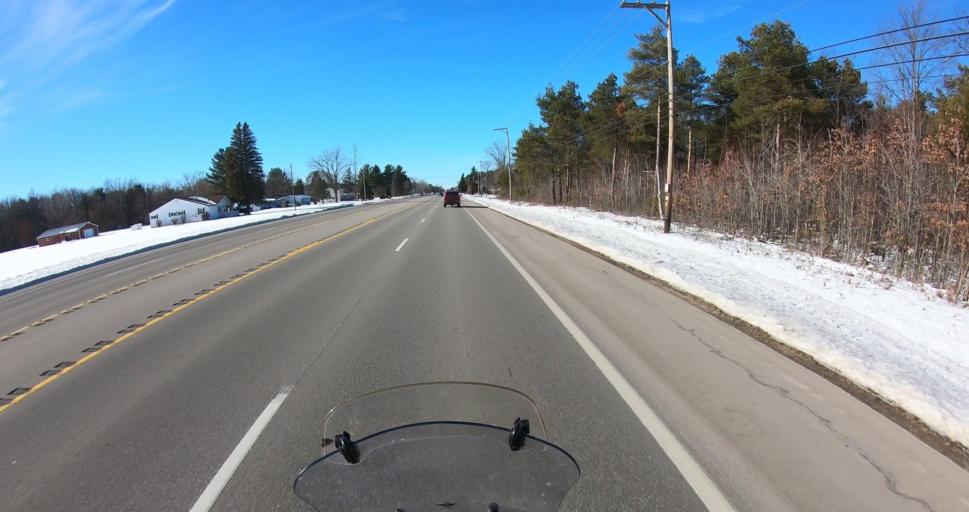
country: US
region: Michigan
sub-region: Isabella County
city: Shepherd
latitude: 43.6122
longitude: -84.6411
